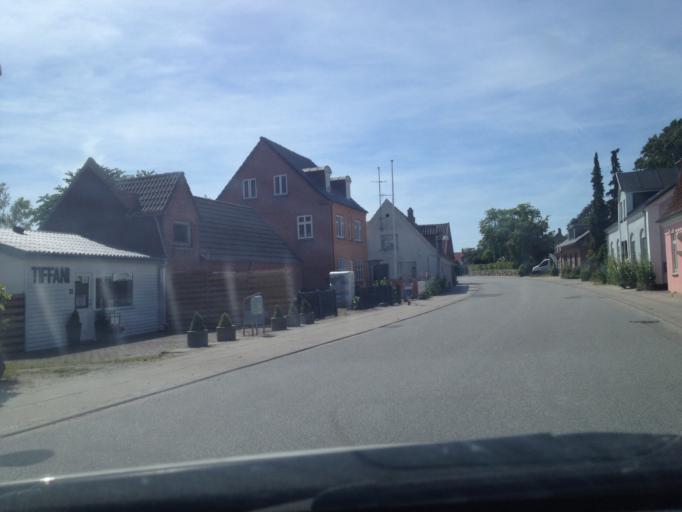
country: DK
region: Central Jutland
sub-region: Samso Kommune
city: Tranebjerg
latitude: 55.8335
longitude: 10.5905
